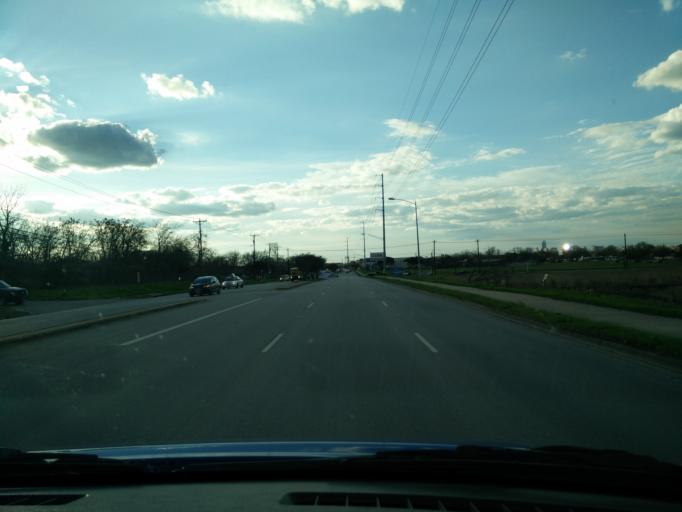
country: US
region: Texas
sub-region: Travis County
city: Austin
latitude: 30.2233
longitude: -97.6993
